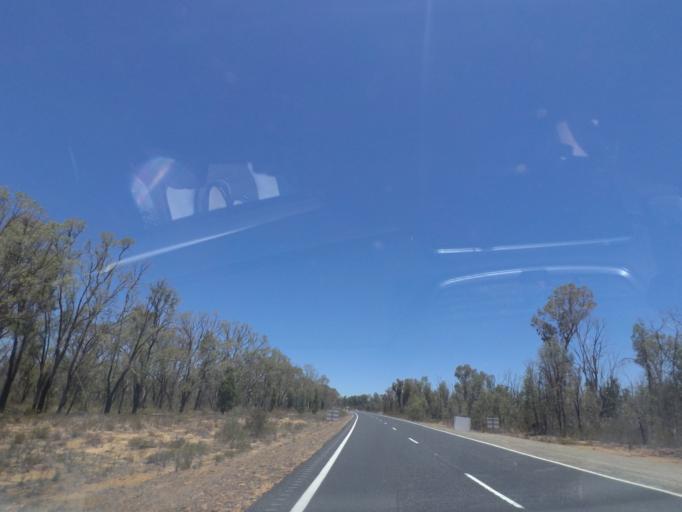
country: AU
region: New South Wales
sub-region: Warrumbungle Shire
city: Coonabarabran
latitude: -30.9424
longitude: 149.4233
